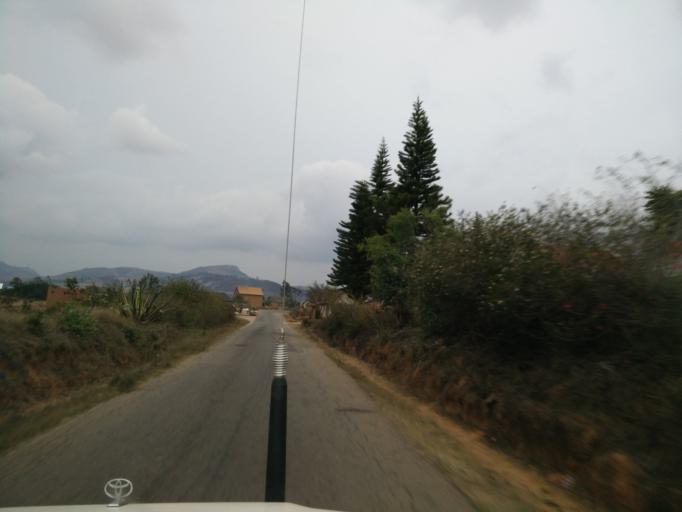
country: MG
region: Upper Matsiatra
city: Fianarantsoa
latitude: -21.5315
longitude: 47.0479
